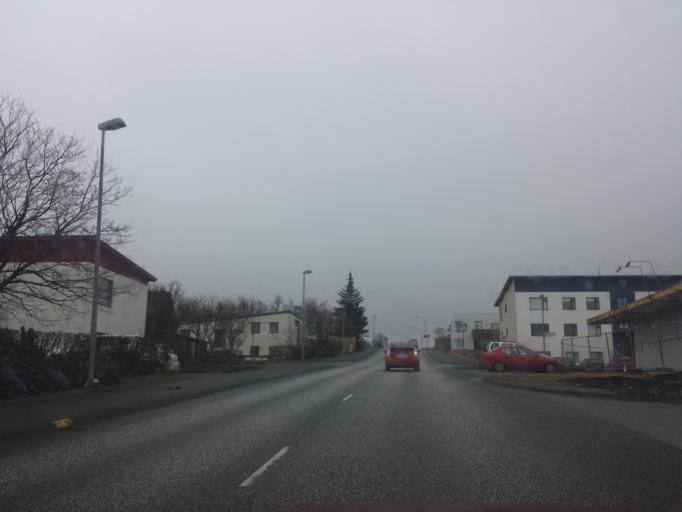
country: IS
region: Capital Region
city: Reykjavik
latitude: 64.1125
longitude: -21.8676
